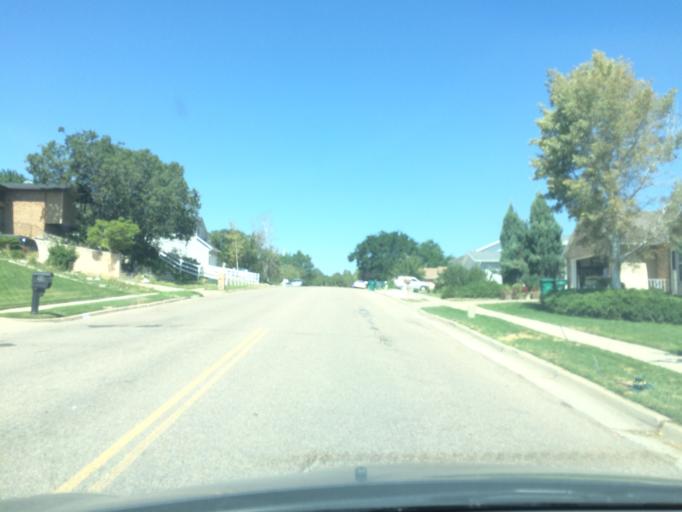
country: US
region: Utah
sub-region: Davis County
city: South Weber
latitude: 41.1072
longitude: -111.9188
